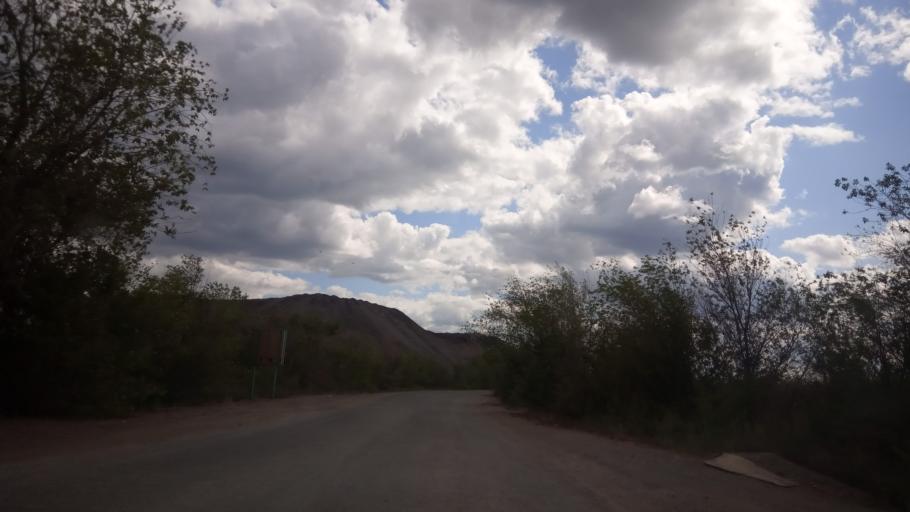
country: RU
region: Orenburg
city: Novotroitsk
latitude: 51.2530
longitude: 58.3667
